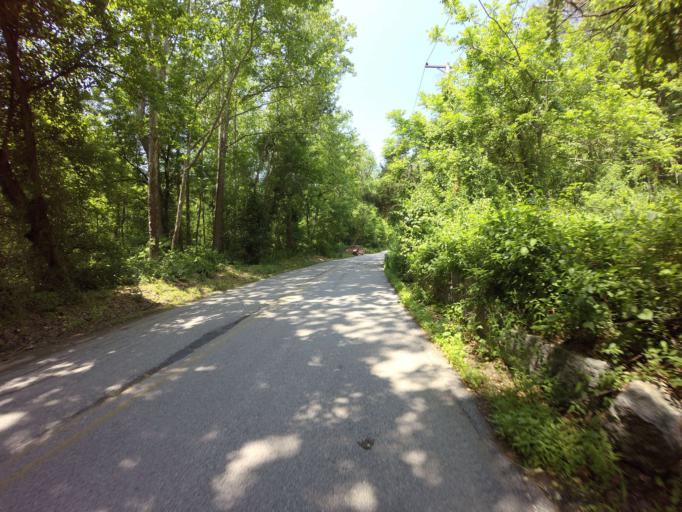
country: US
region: Maryland
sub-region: Howard County
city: Ilchester
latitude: 39.2574
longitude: -76.7798
